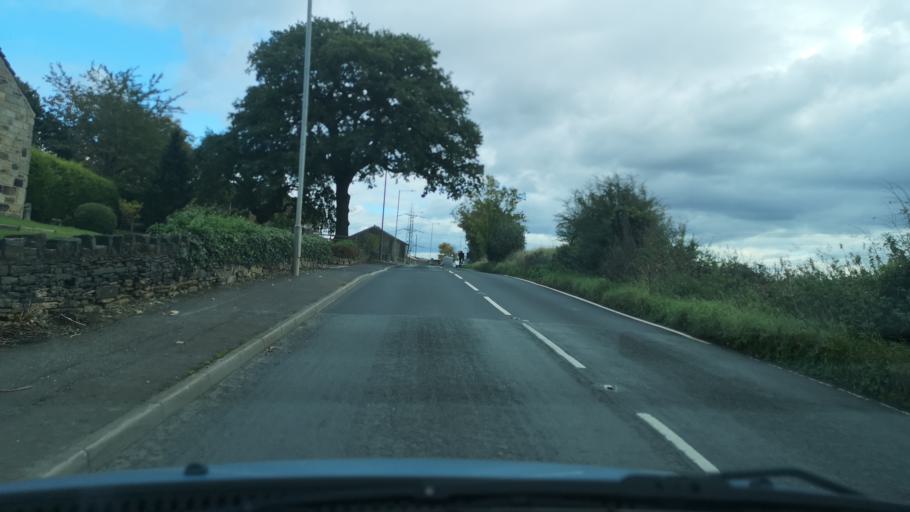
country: GB
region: England
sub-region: City and Borough of Wakefield
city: Middlestown
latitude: 53.6613
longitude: -1.5940
